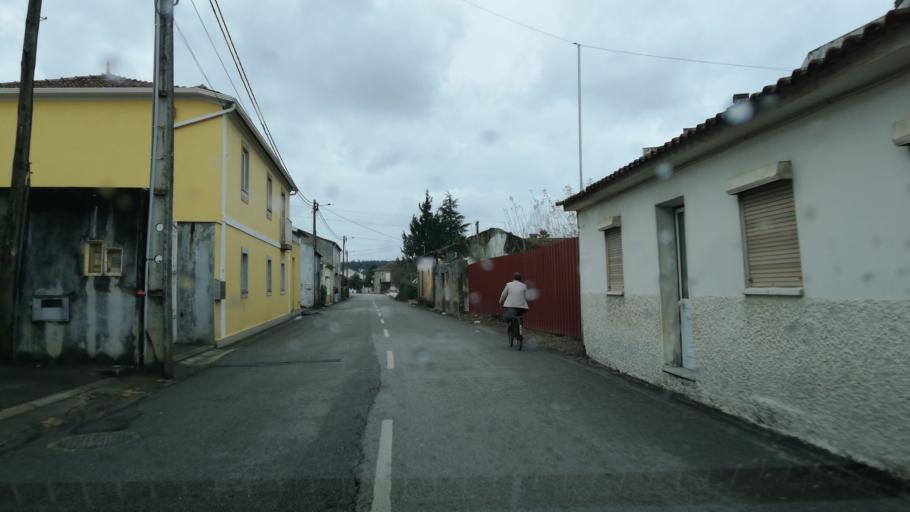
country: PT
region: Aveiro
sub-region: Agueda
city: Valongo
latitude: 40.6175
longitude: -8.4299
